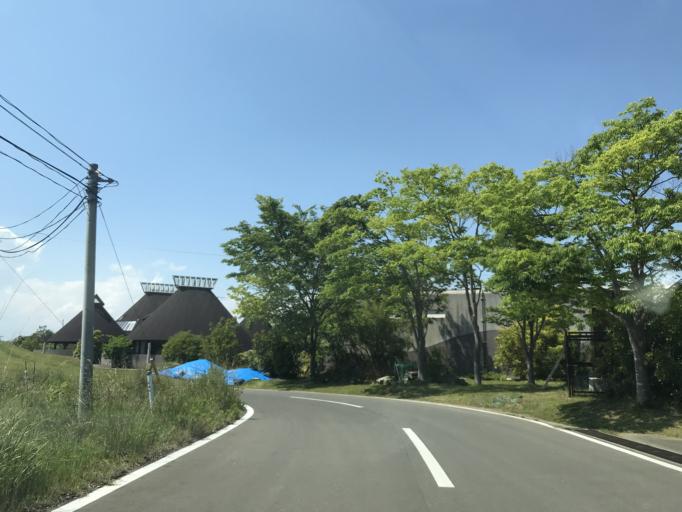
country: JP
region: Miyagi
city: Matsushima
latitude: 38.3373
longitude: 141.1474
